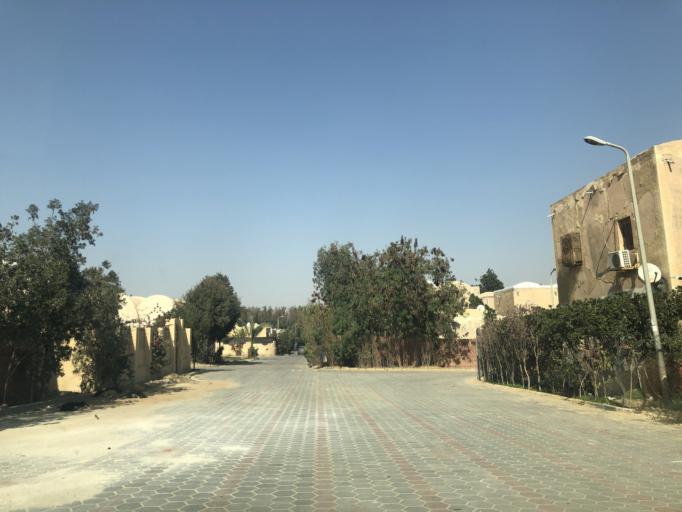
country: EG
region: Al Jizah
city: Madinat Sittah Uktubar
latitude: 29.9553
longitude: 31.0079
